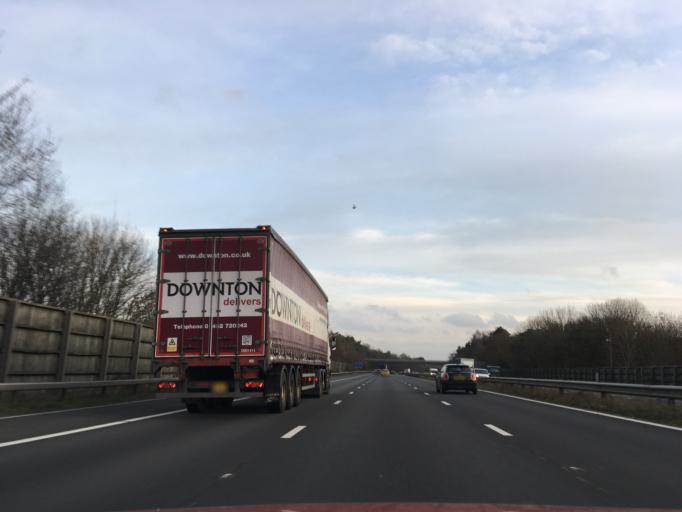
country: GB
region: England
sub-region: Gloucestershire
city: Barnwood
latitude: 51.8327
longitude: -2.2052
